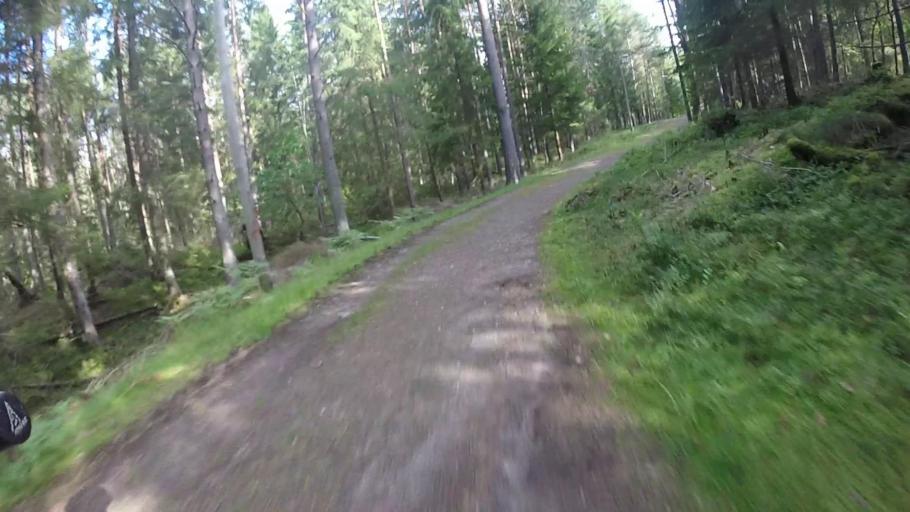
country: SE
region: Vaestra Goetaland
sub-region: Trollhattan
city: Trollhattan
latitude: 58.2547
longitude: 12.2469
